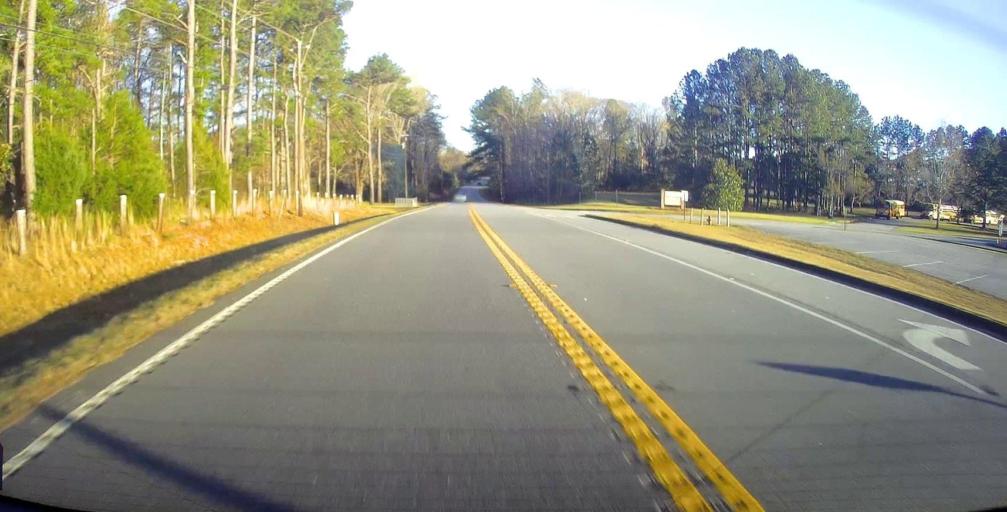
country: US
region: Georgia
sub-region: Harris County
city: Hamilton
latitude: 32.6317
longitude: -84.8259
